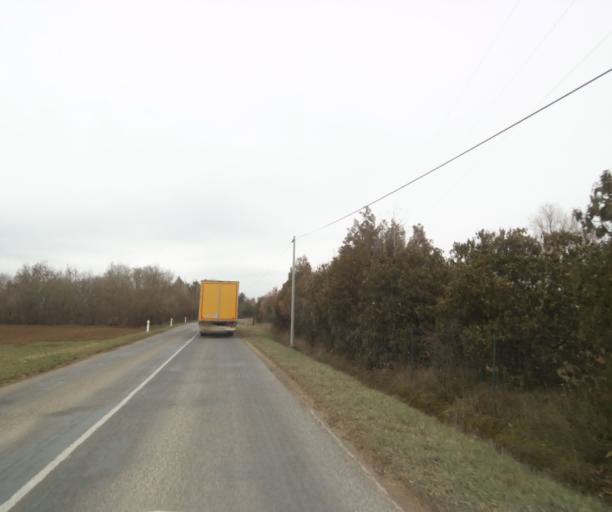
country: FR
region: Champagne-Ardenne
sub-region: Departement de la Haute-Marne
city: Villiers-en-Lieu
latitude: 48.6489
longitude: 4.9064
